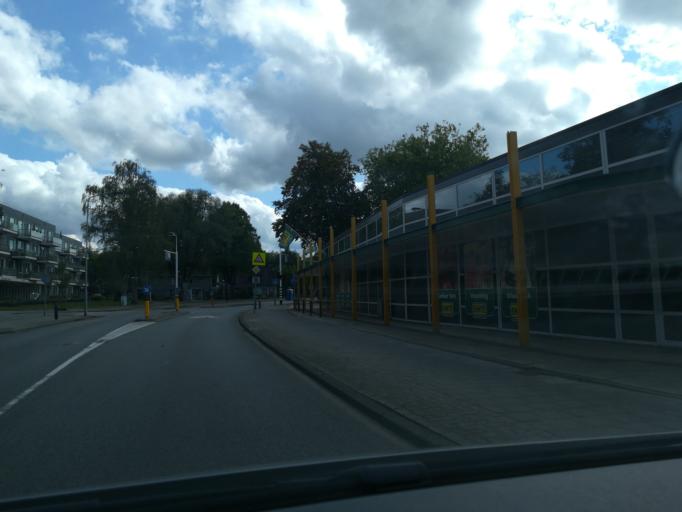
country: NL
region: North Brabant
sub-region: Gemeente Valkenswaard
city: Valkenswaard
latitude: 51.3608
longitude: 5.4479
